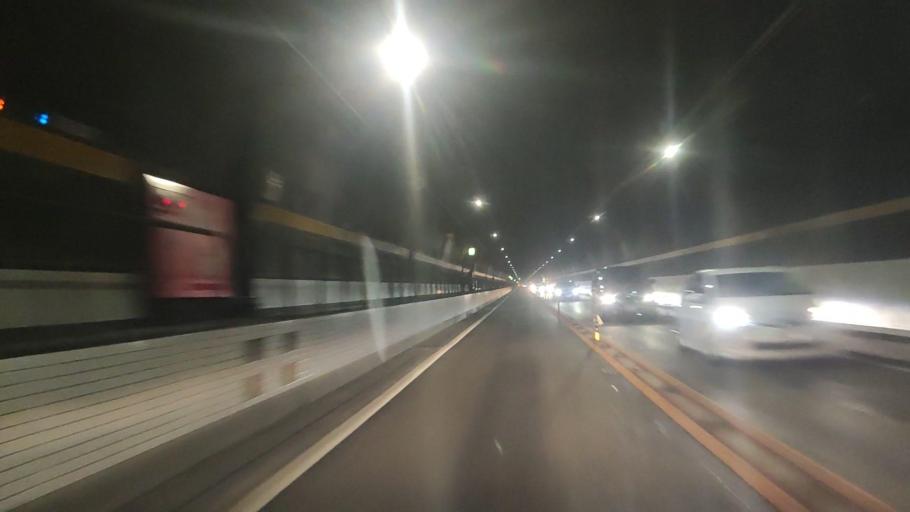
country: JP
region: Nagasaki
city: Obita
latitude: 32.7862
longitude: 129.8829
